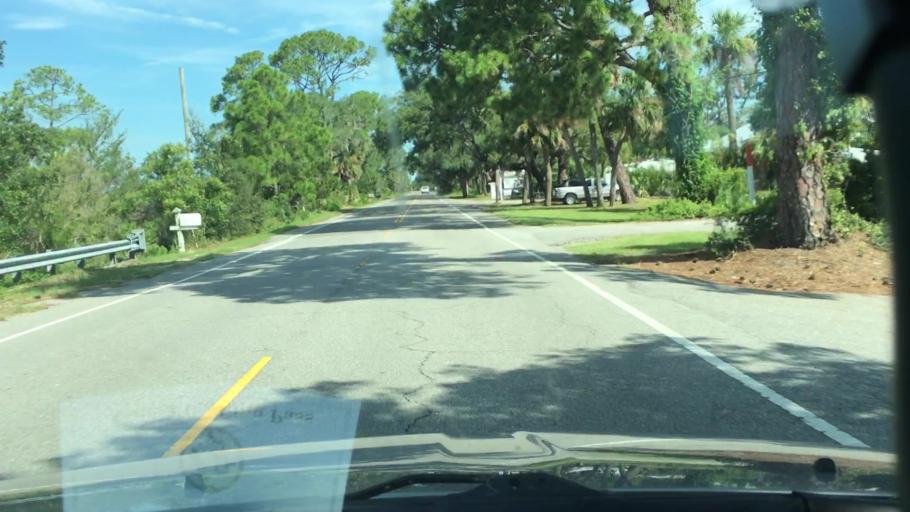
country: US
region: South Carolina
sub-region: Beaufort County
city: Beaufort
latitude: 32.3965
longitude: -80.4419
